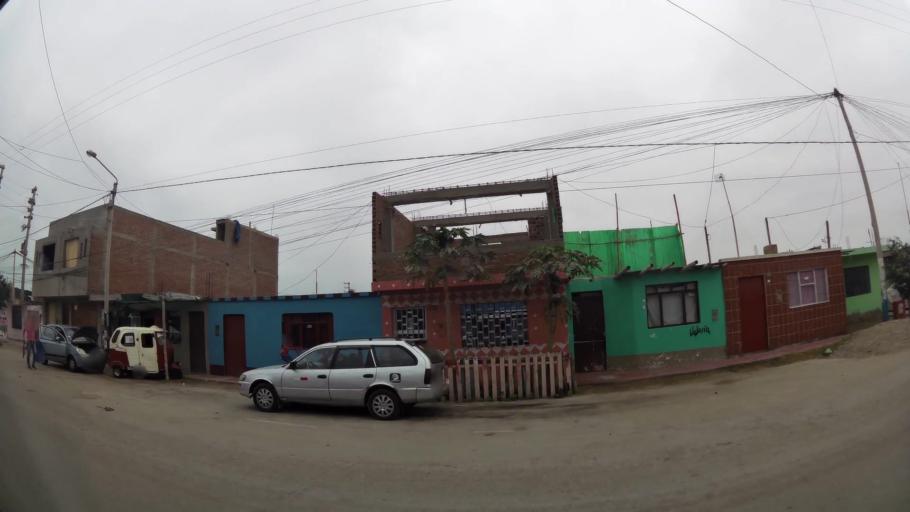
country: PE
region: Ica
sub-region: Provincia de Pisco
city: Pisco
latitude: -13.7338
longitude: -76.2179
